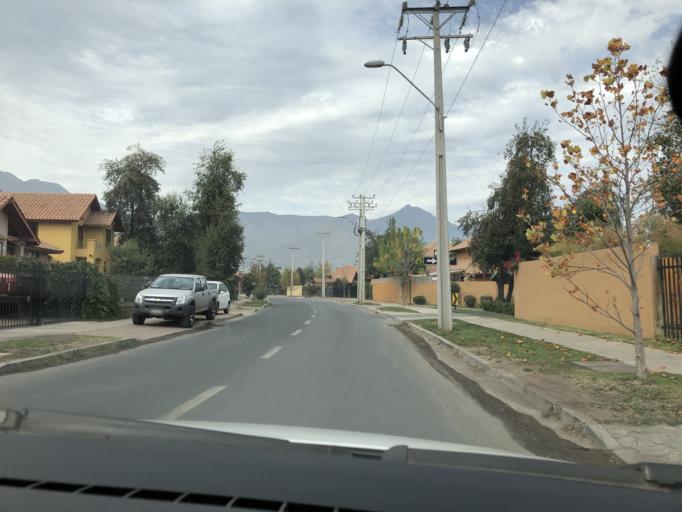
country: CL
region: Santiago Metropolitan
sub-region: Provincia de Cordillera
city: Puente Alto
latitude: -33.5857
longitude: -70.5135
